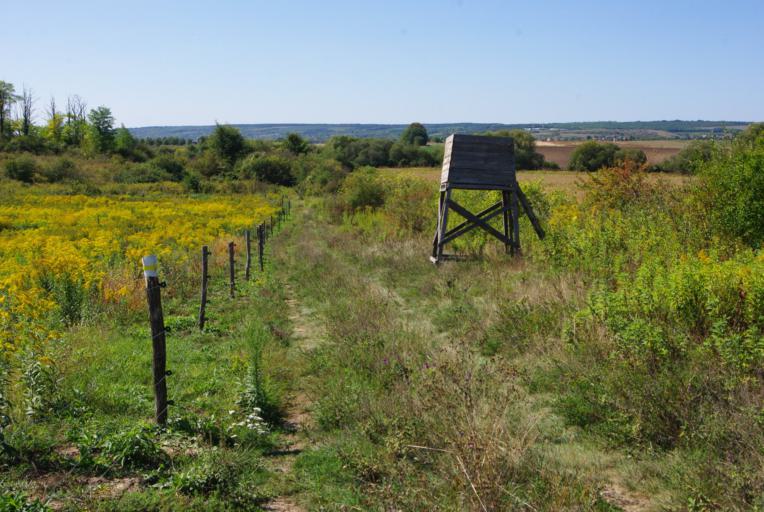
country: HU
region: Pest
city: Perbal
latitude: 47.5934
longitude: 18.7891
